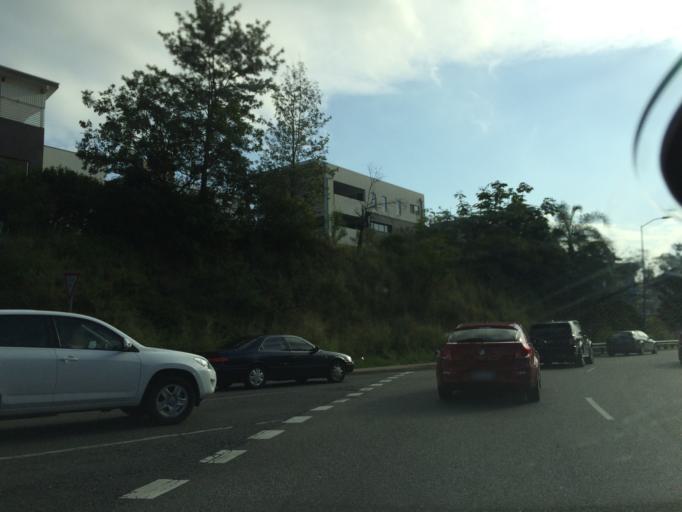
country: AU
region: Queensland
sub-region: Brisbane
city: Taringa
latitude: -27.4974
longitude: 152.9755
